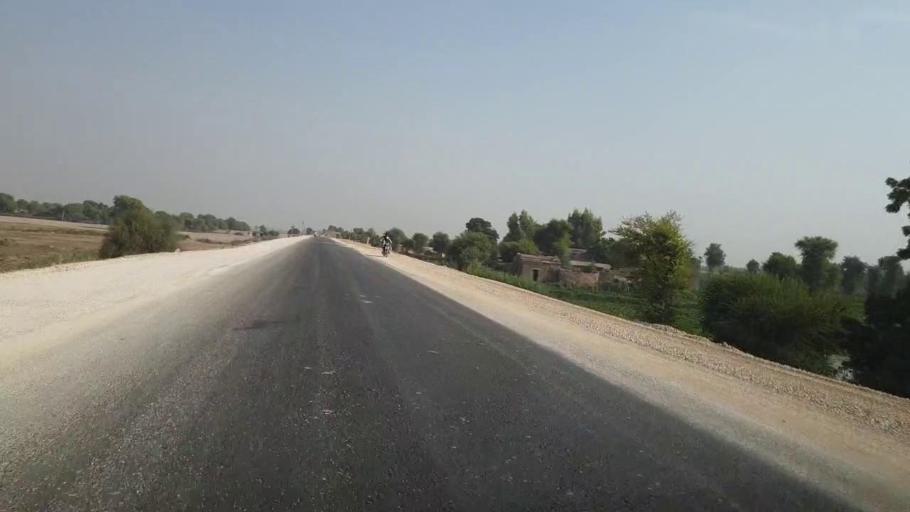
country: PK
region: Sindh
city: Bhan
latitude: 26.5493
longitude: 67.7845
